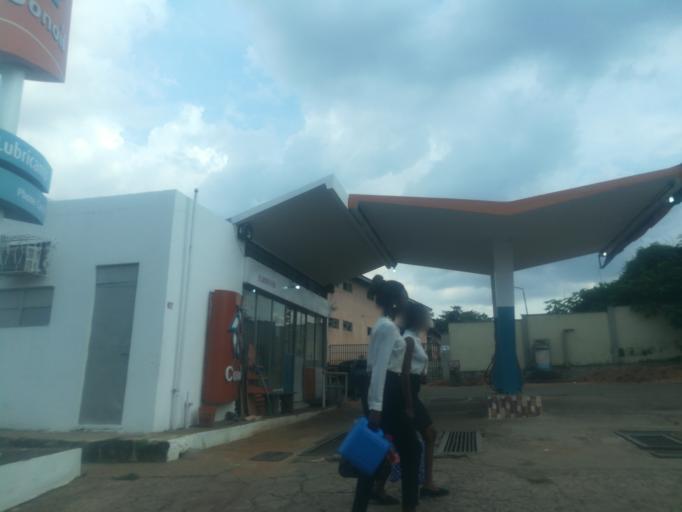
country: NG
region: Oyo
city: Ibadan
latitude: 7.4519
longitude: 3.9011
